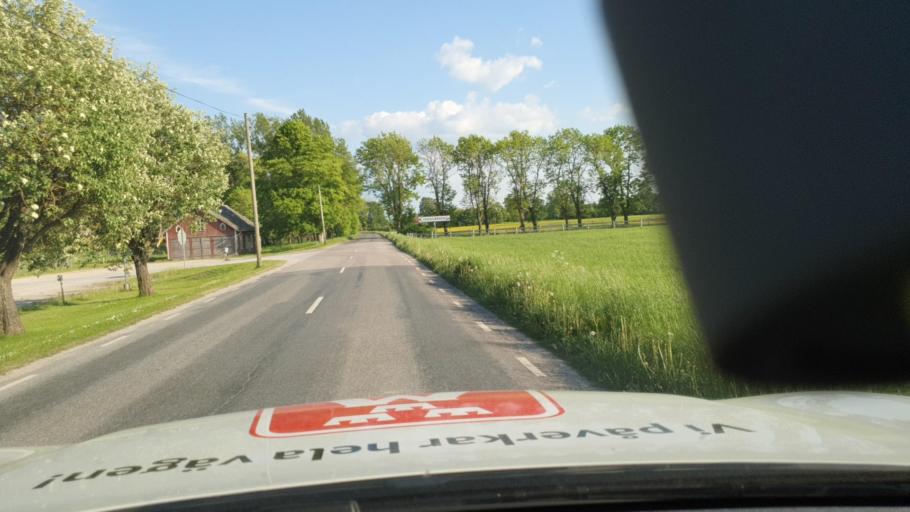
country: SE
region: Vaestra Goetaland
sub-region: Falkopings Kommun
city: Akarp
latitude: 58.1859
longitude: 13.6297
